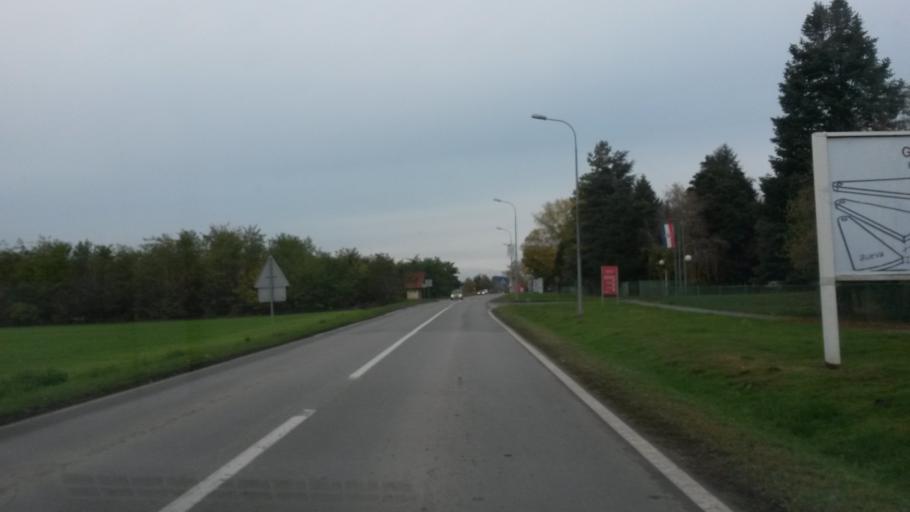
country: HR
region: Osjecko-Baranjska
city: Beli Manastir
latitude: 45.7607
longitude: 18.6267
